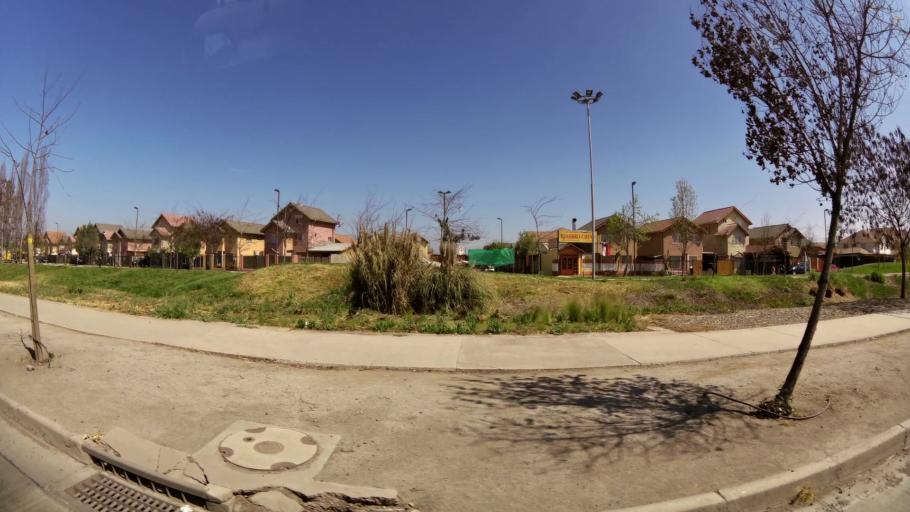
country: CL
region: Santiago Metropolitan
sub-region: Provincia de Chacabuco
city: Chicureo Abajo
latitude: -33.3272
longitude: -70.7463
